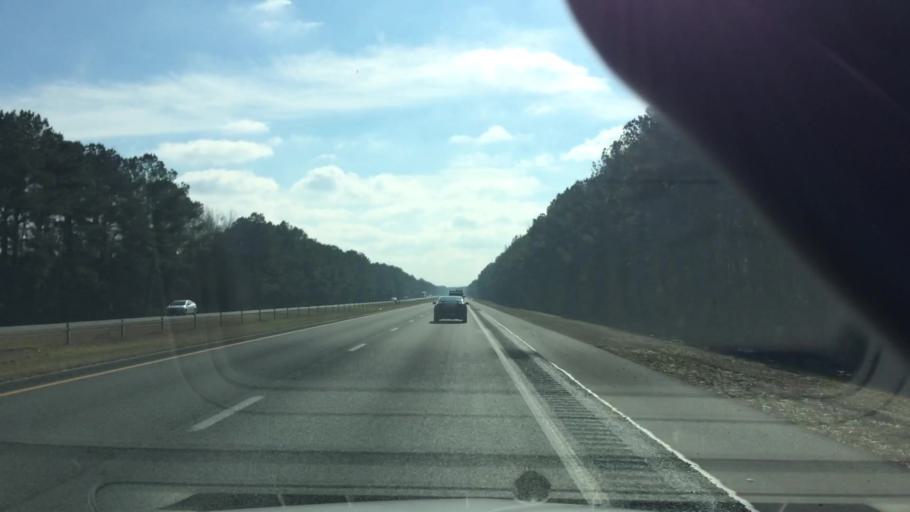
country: US
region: North Carolina
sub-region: Duplin County
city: Wallace
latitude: 34.7293
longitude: -77.9450
